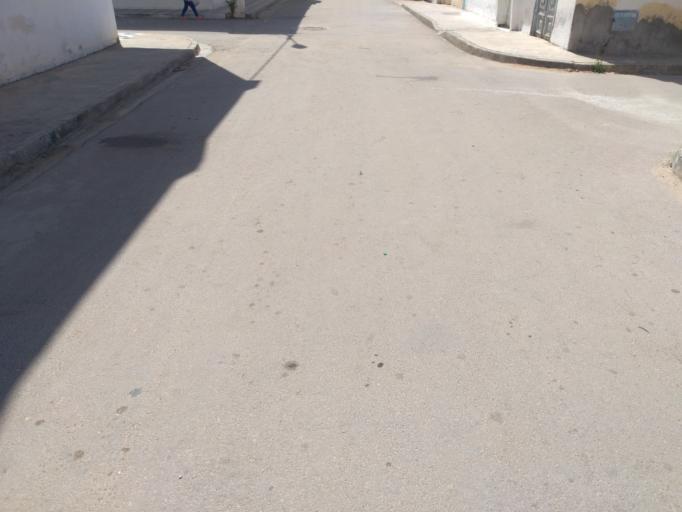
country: TN
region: Al Qayrawan
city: Kairouan
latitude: 35.6672
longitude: 10.0816
